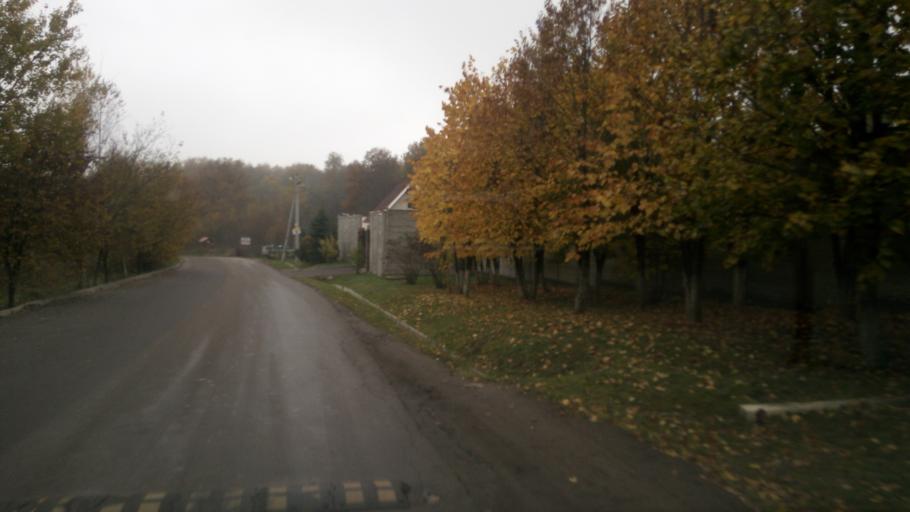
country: RU
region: Moskovskaya
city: Skhodnya
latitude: 55.9334
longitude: 37.2786
